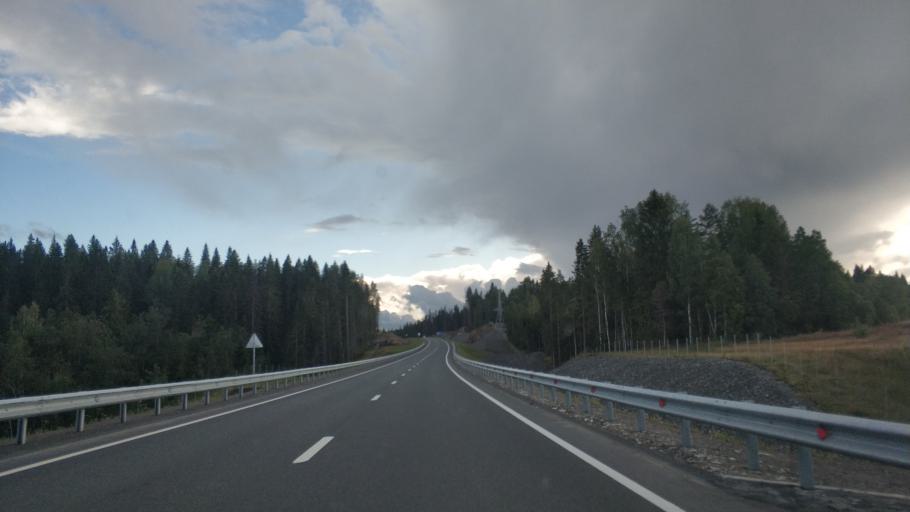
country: RU
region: Republic of Karelia
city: Lakhdenpokh'ya
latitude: 61.4712
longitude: 30.0049
